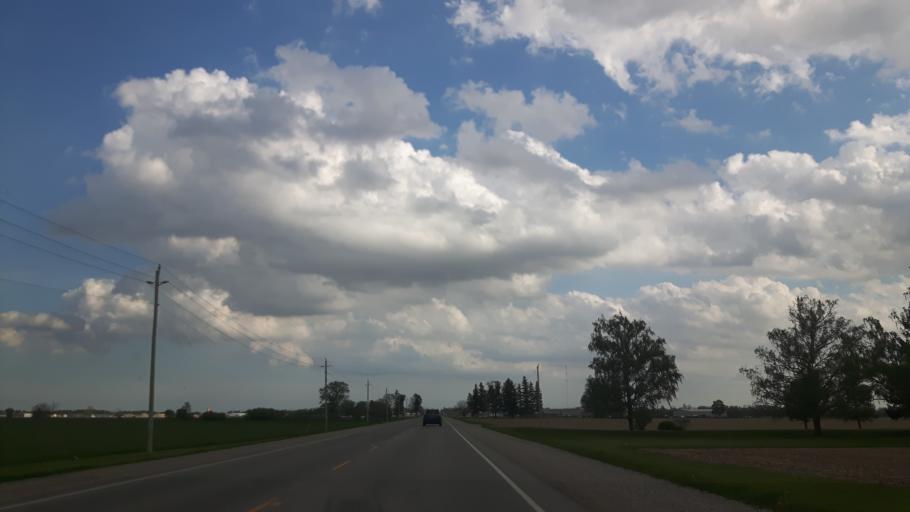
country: CA
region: Ontario
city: South Huron
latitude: 43.3753
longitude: -81.4864
